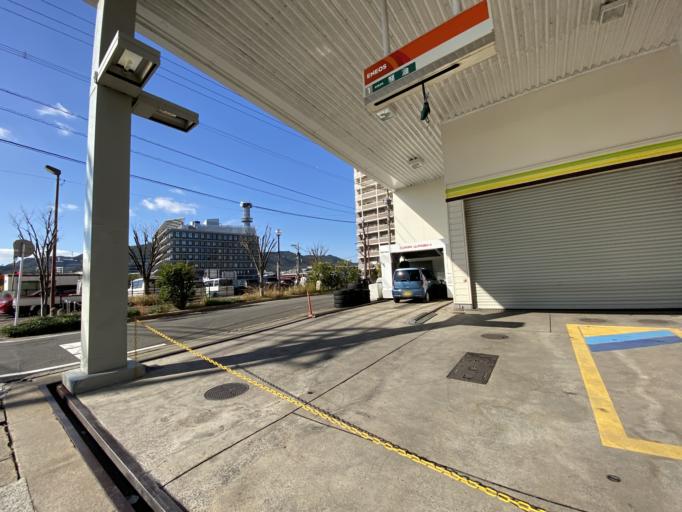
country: JP
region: Nagasaki
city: Nagasaki-shi
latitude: 32.7493
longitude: 129.8721
